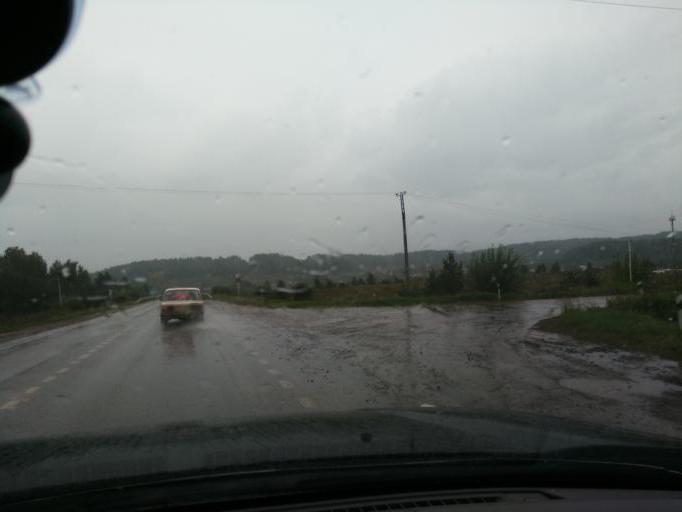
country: RU
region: Perm
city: Osa
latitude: 57.1951
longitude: 55.5917
